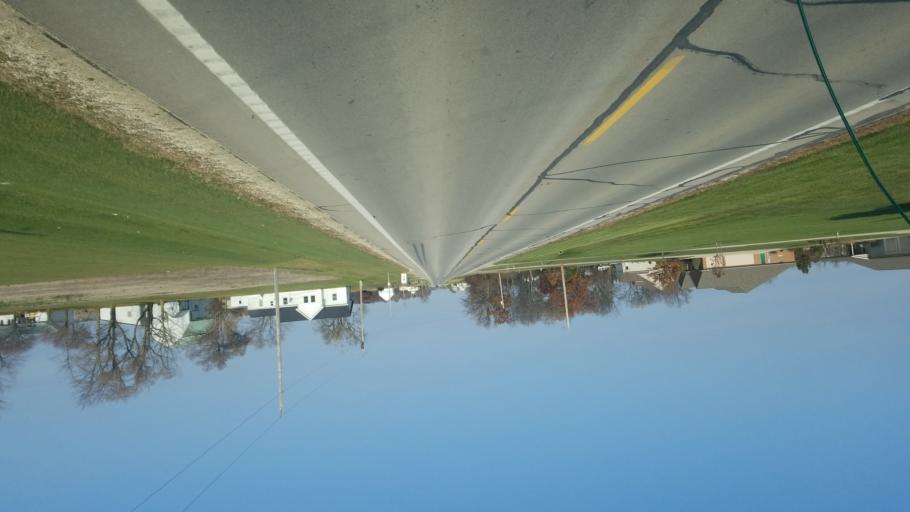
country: US
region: Ohio
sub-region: Mercer County
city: Coldwater
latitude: 40.5240
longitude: -84.6286
